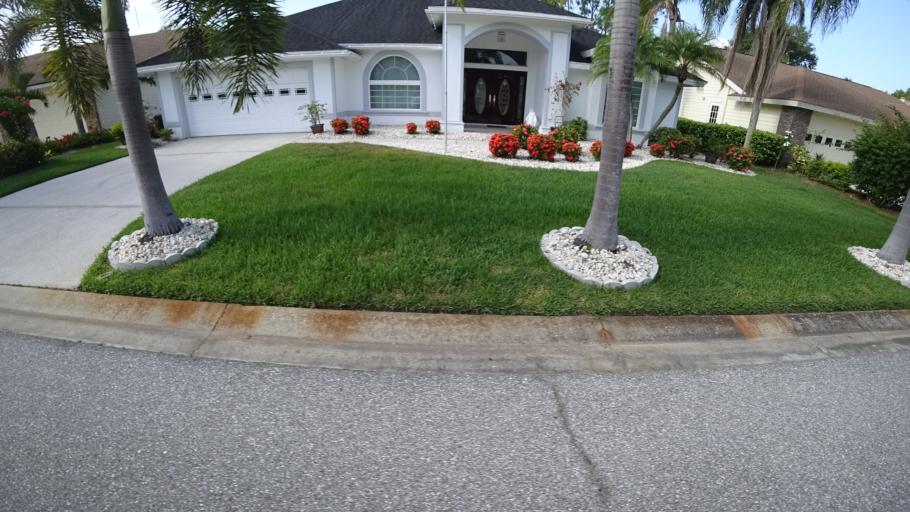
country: US
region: Florida
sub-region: Sarasota County
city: North Sarasota
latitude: 27.3973
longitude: -82.5032
